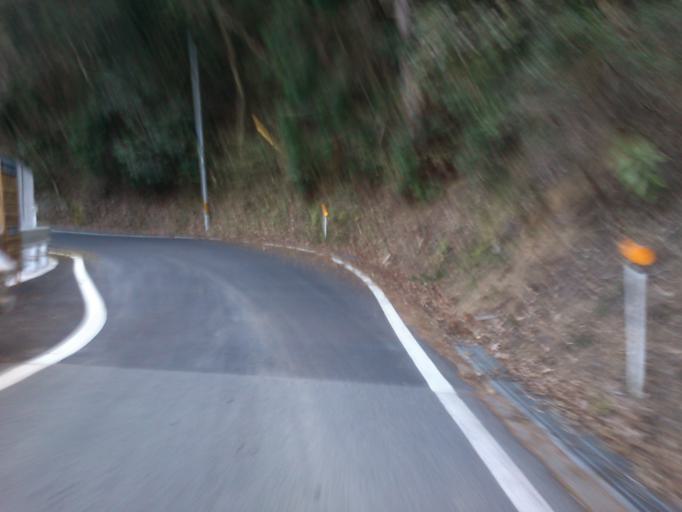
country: JP
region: Kyoto
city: Yawata
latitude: 34.9159
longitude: 135.6490
